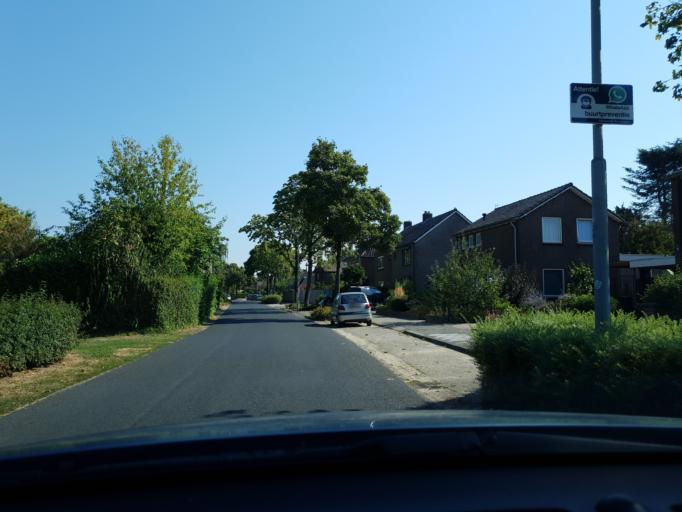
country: NL
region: Gelderland
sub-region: Gemeente Nijmegen
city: Lindenholt
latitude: 51.8544
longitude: 5.8093
